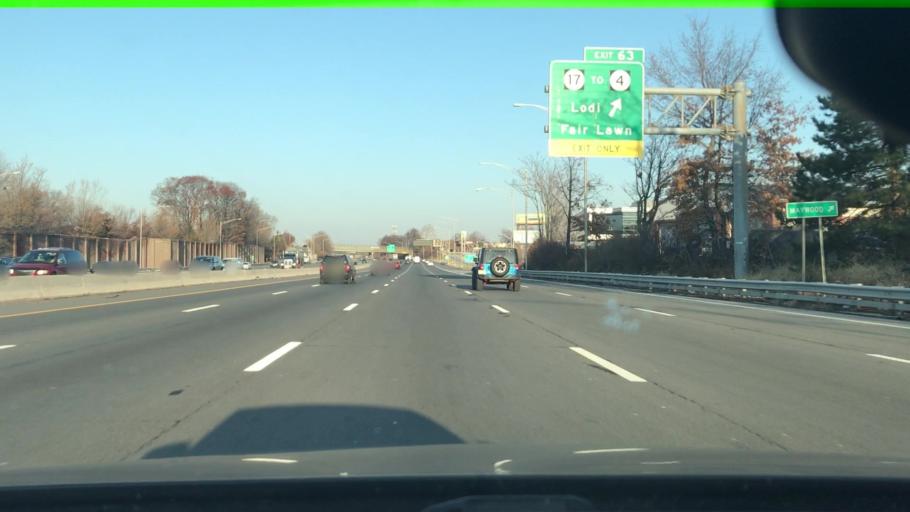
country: US
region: New Jersey
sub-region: Bergen County
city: Lodi
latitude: 40.8891
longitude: -74.0716
